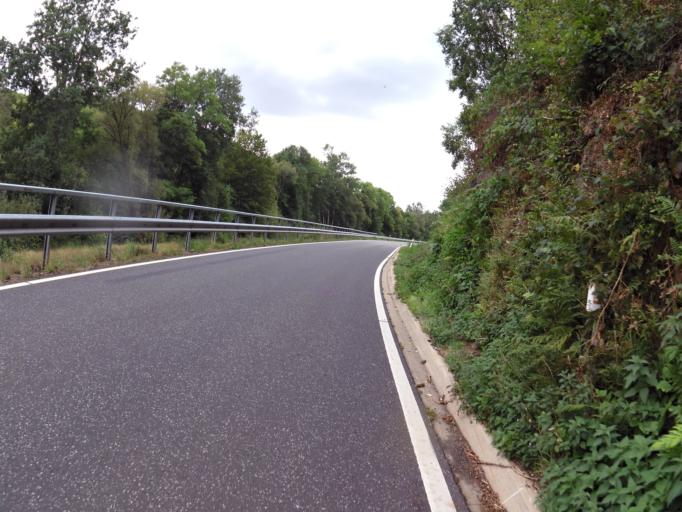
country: DE
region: Rheinland-Pfalz
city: Zendscheid
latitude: 50.0962
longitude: 6.6034
